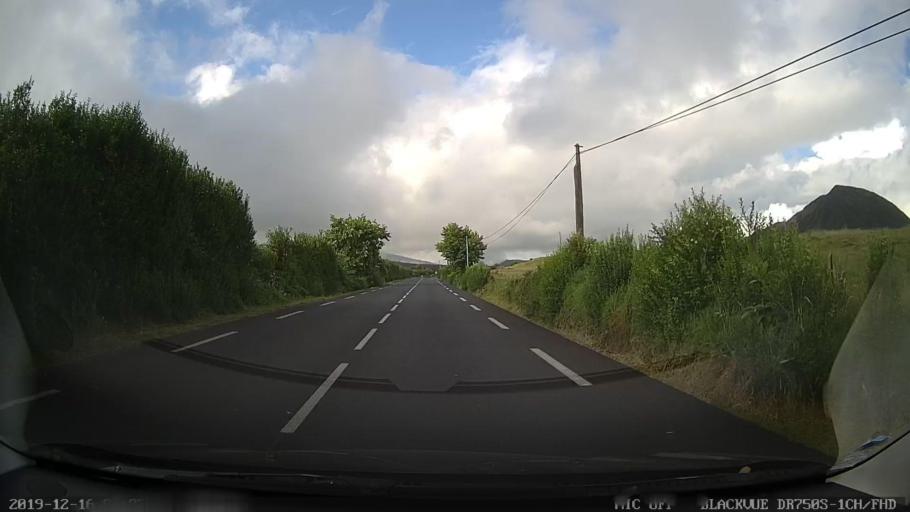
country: RE
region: Reunion
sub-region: Reunion
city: Cilaos
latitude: -21.1814
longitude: 55.5794
